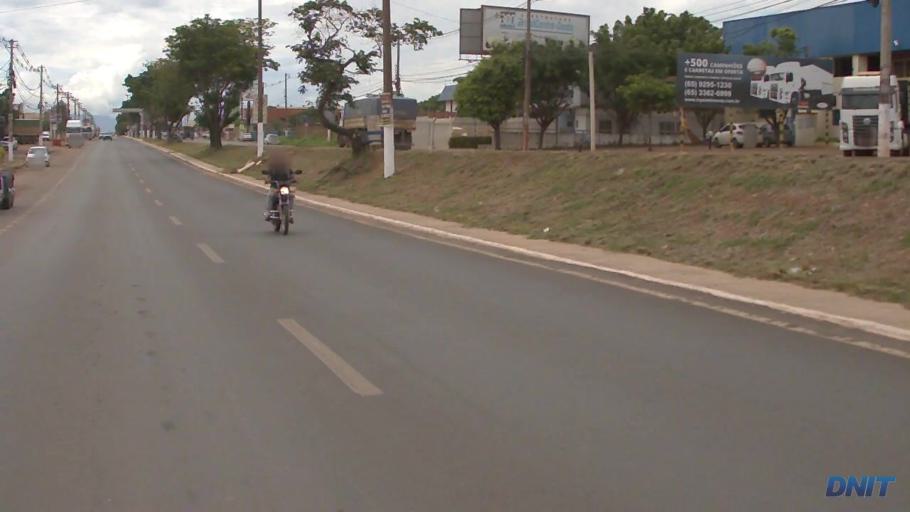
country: BR
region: Mato Grosso
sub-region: Varzea Grande
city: Varzea Grande
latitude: -15.6473
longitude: -56.1904
